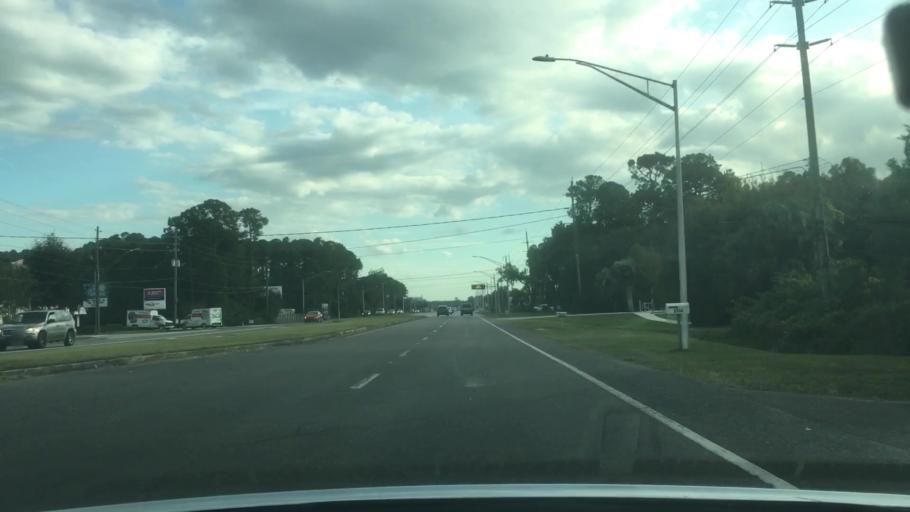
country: US
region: Florida
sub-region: Duval County
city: Neptune Beach
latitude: 30.2948
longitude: -81.5260
